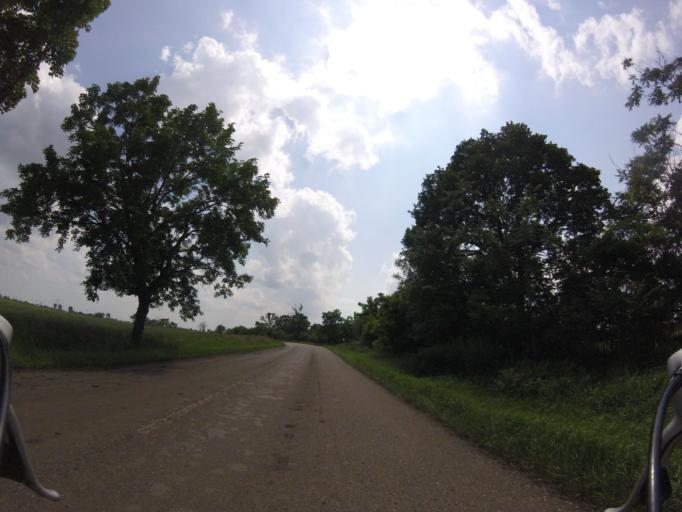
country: HU
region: Heves
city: Kiskore
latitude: 47.5725
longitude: 20.4142
